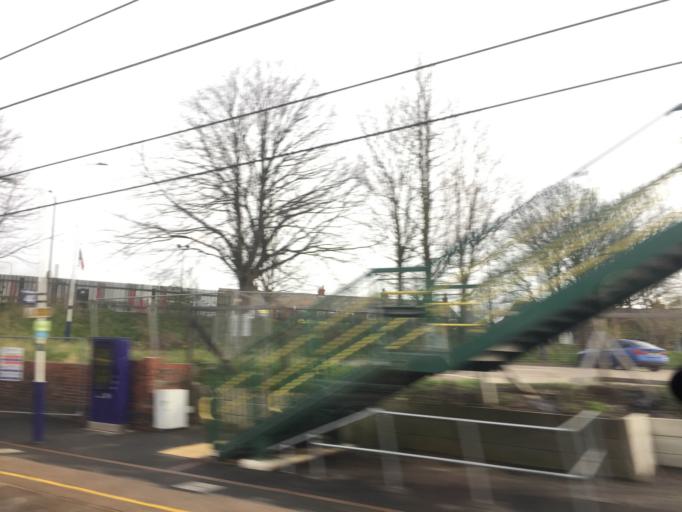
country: GB
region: England
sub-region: Lancashire
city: Leyland
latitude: 53.6984
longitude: -2.6865
